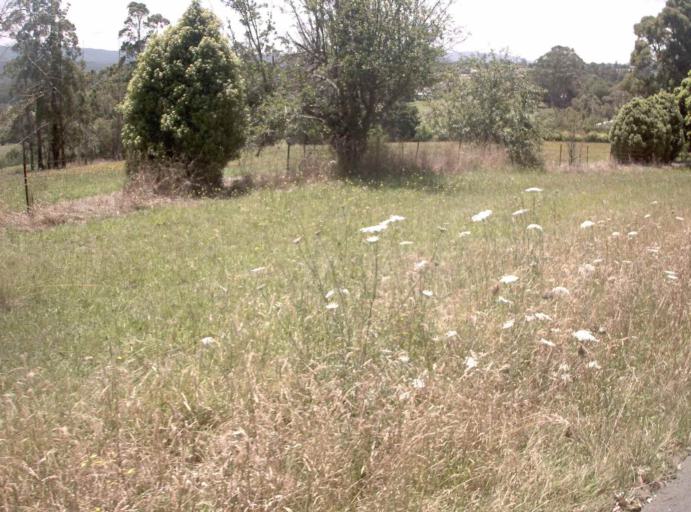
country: AU
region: Victoria
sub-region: Baw Baw
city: Warragul
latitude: -38.0301
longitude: 145.9549
